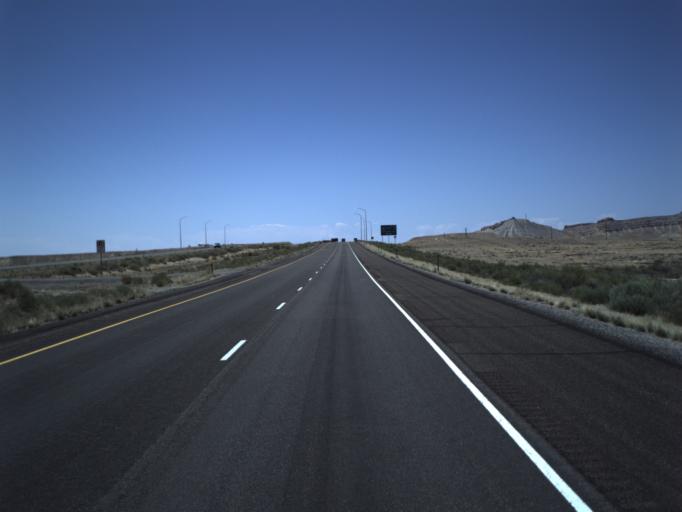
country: US
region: Utah
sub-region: Grand County
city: Moab
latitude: 38.9443
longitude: -109.8053
